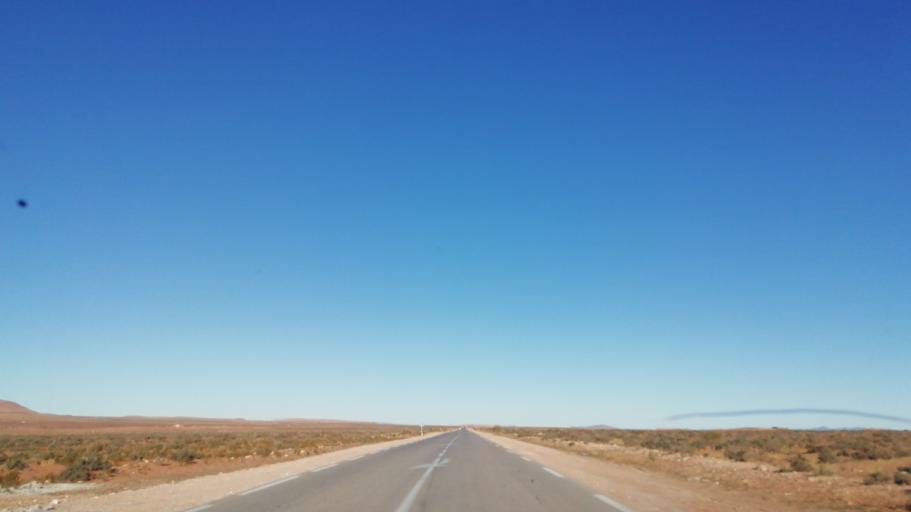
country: DZ
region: El Bayadh
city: El Abiodh Sidi Cheikh
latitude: 33.1138
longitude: 0.2633
